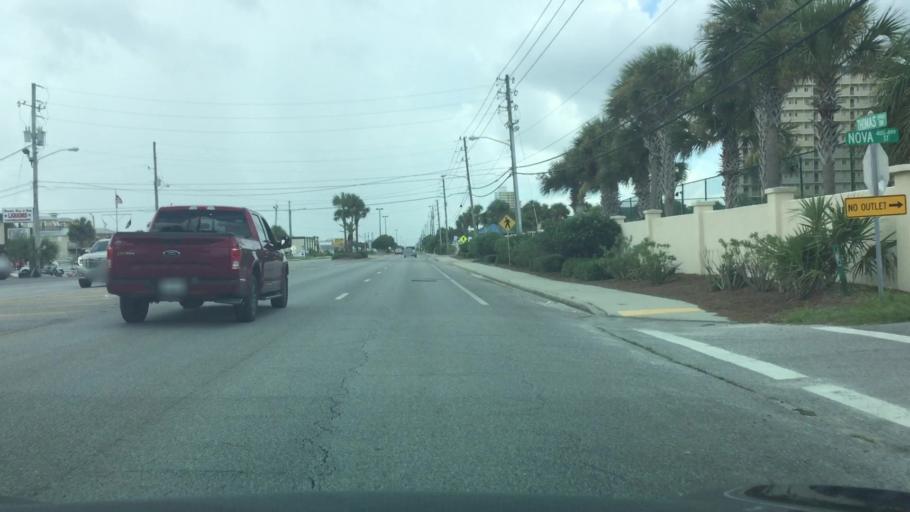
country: US
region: Florida
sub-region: Bay County
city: Lower Grand Lagoon
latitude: 30.1482
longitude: -85.7617
